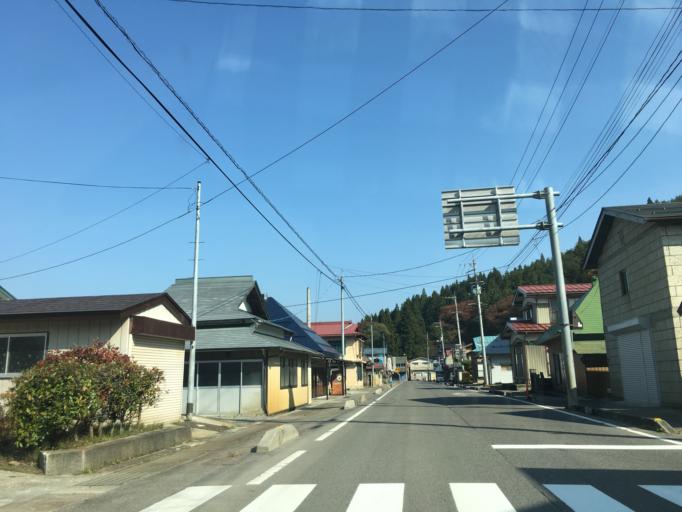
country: JP
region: Fukushima
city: Inawashiro
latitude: 37.3909
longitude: 140.0883
